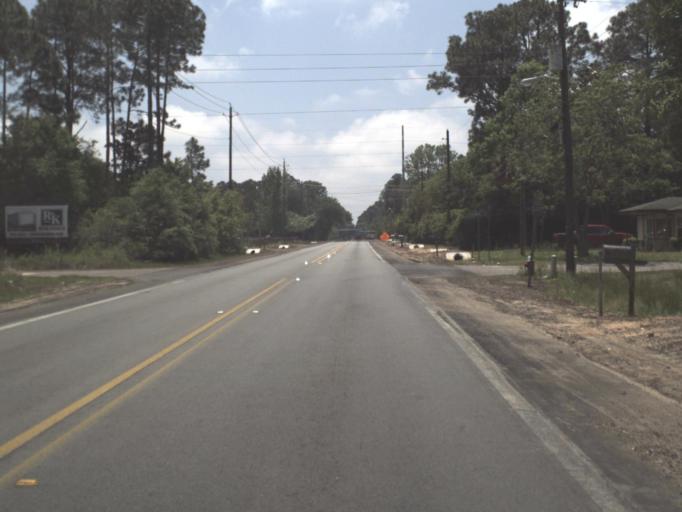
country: US
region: Florida
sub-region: Escambia County
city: Warrington
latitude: 30.3853
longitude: -87.3080
